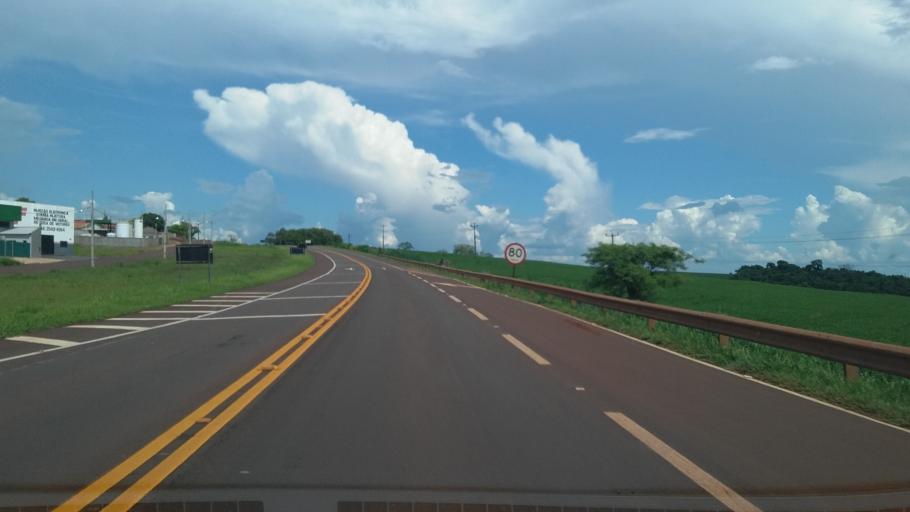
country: BR
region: Parana
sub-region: Corbelia
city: Corbelia
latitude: -24.5573
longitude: -52.9975
